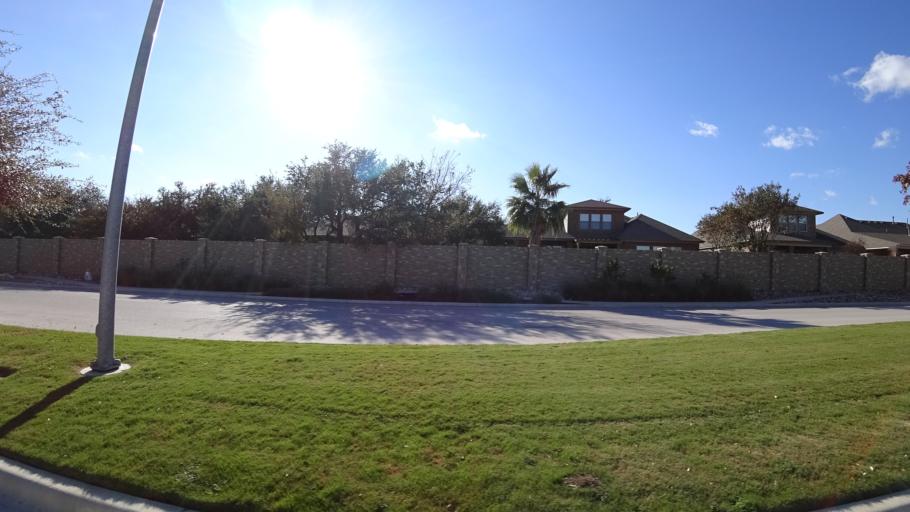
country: US
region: Texas
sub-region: Williamson County
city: Brushy Creek
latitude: 30.4887
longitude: -97.7214
